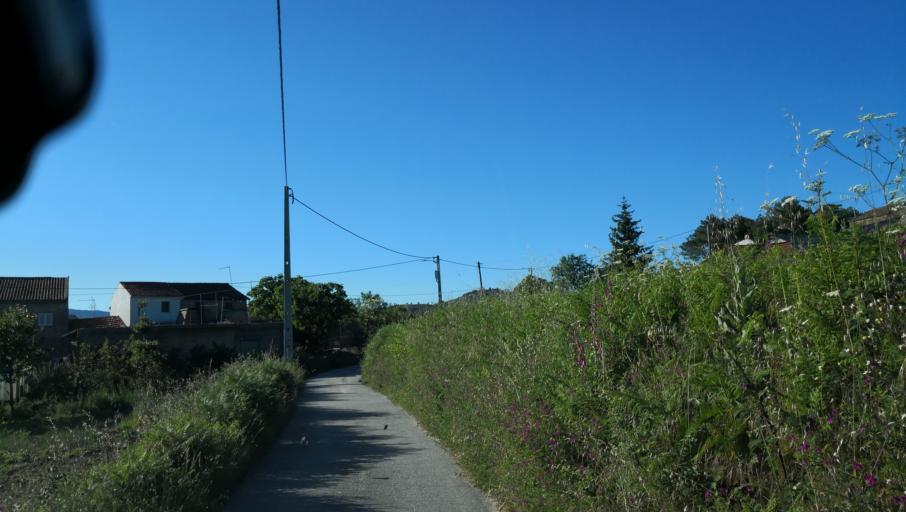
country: PT
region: Vila Real
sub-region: Vila Real
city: Vila Real
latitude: 41.3248
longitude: -7.6748
